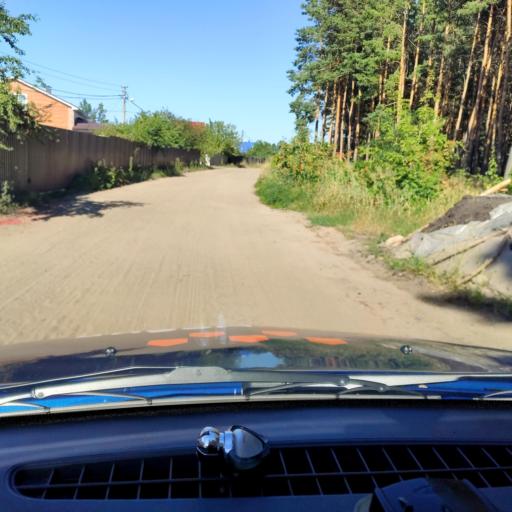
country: RU
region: Voronezj
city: Maslovka
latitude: 51.5471
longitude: 39.1812
